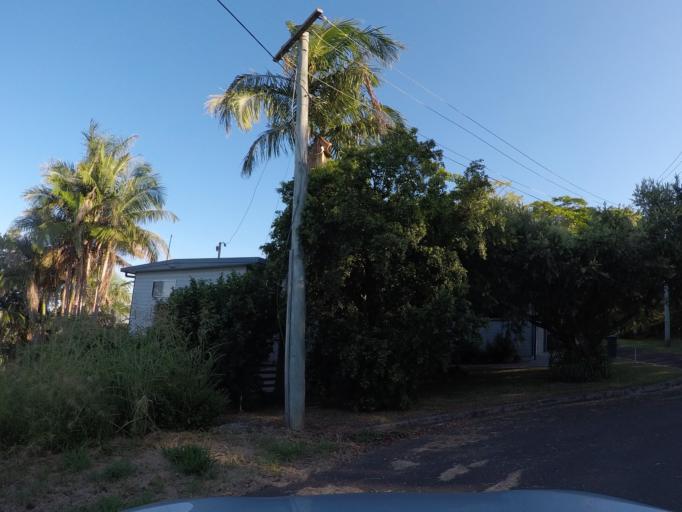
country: AU
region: Queensland
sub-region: Sunshine Coast
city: Nambour
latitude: -26.6371
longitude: 152.8697
